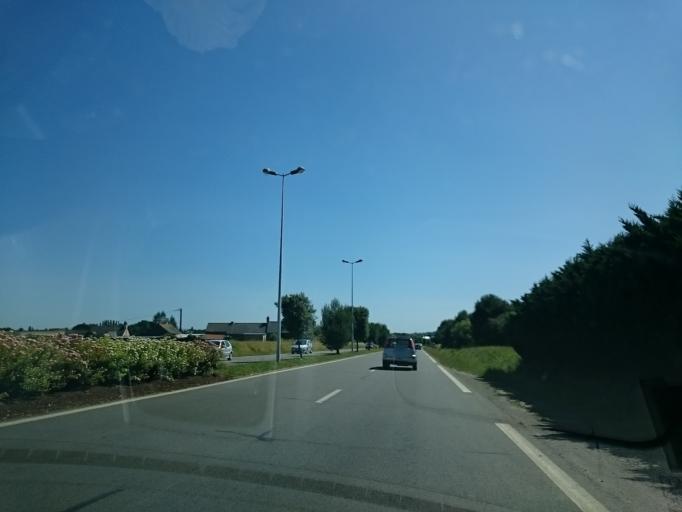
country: FR
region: Brittany
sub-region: Departement d'Ille-et-Vilaine
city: Saint-Malo
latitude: 48.6573
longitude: -1.9672
